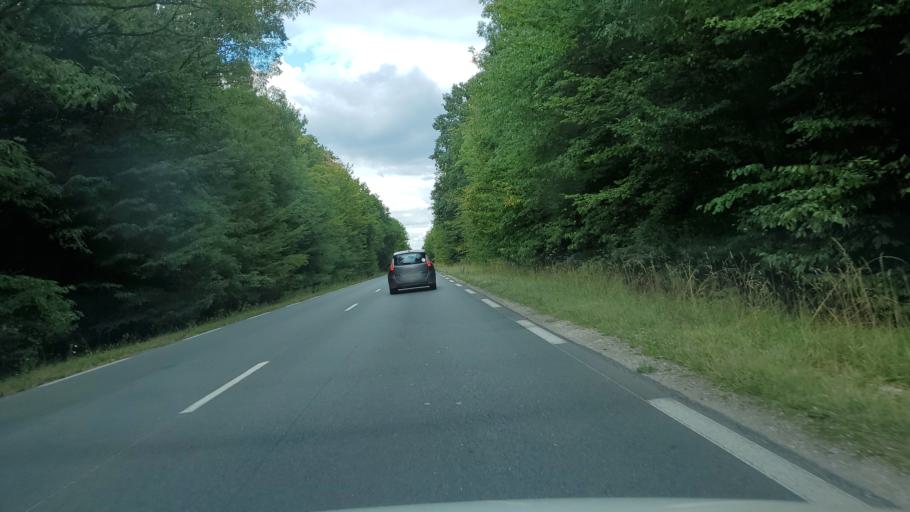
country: FR
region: Ile-de-France
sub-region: Departement de Seine-et-Marne
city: La Houssaye-en-Brie
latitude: 48.7883
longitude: 2.8755
